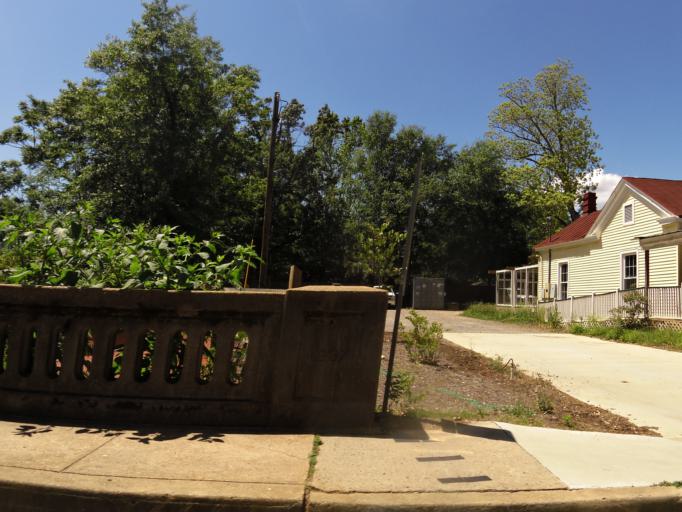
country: US
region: South Carolina
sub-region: Aiken County
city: Aiken
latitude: 33.5575
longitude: -81.7209
